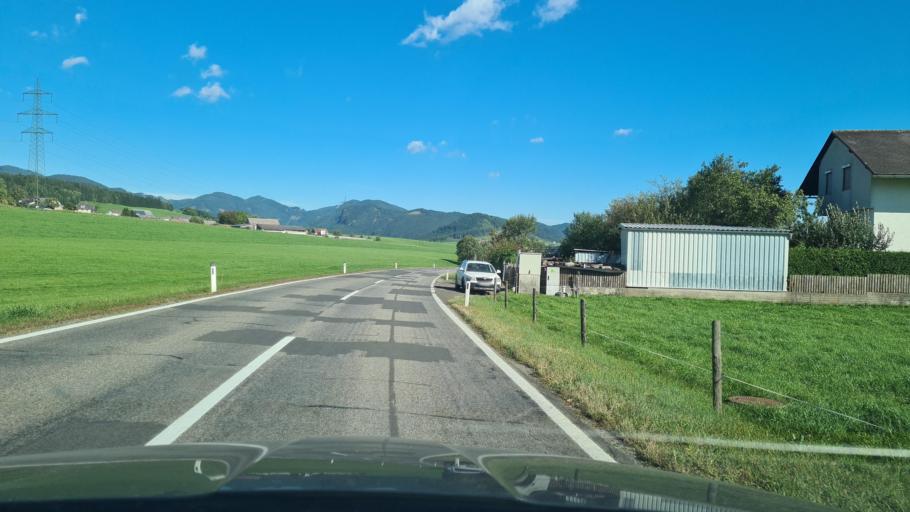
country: AT
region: Styria
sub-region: Politischer Bezirk Leoben
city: Traboch
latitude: 47.4094
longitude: 14.9608
